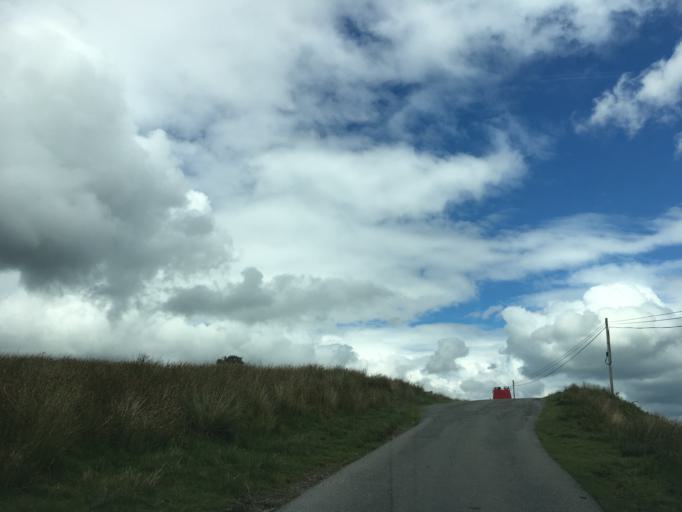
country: GB
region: Scotland
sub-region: Argyll and Bute
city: Oban
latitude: 56.3280
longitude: -5.2153
